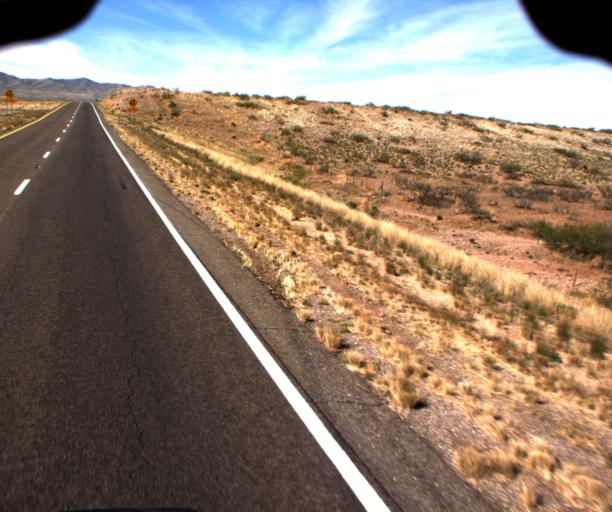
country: US
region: Arizona
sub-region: Cochise County
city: Willcox
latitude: 32.3708
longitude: -109.6751
